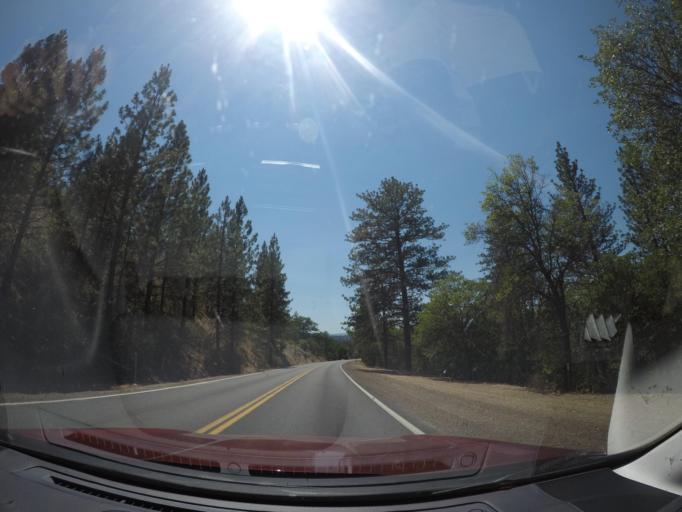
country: US
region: California
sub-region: Shasta County
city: Burney
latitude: 40.9841
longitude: -121.5202
